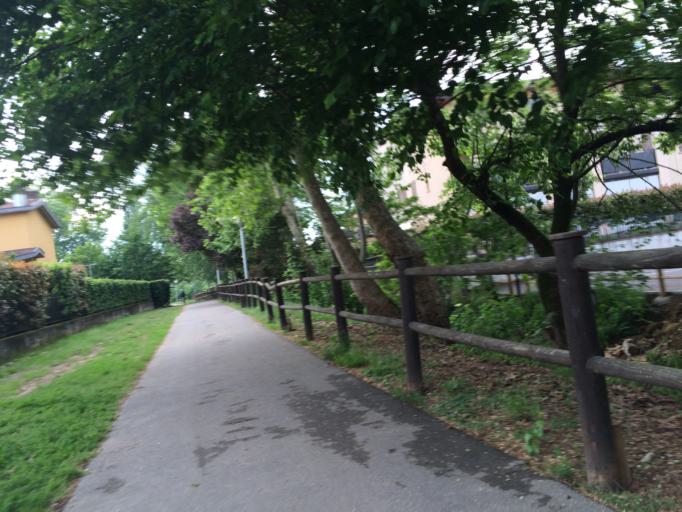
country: IT
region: Lombardy
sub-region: Provincia di Brescia
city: Flero
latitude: 45.4804
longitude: 10.1757
